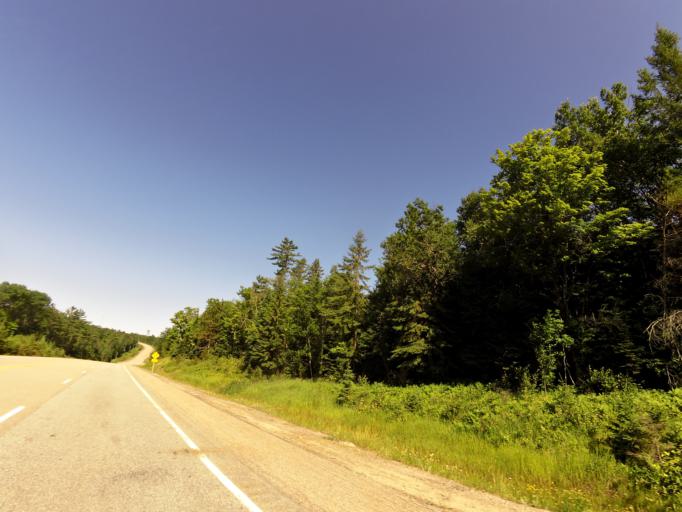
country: CA
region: Ontario
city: Mattawa
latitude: 46.2429
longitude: -78.1171
